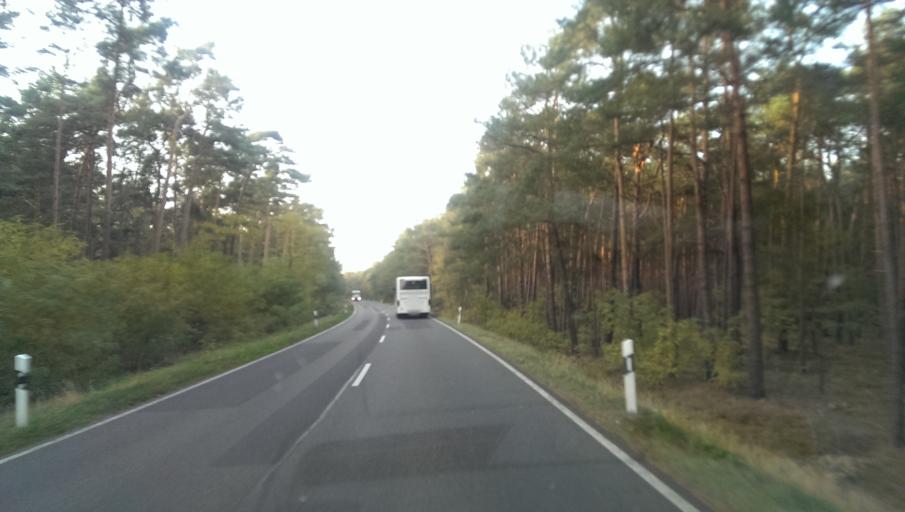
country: DE
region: Saxony-Anhalt
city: Holzdorf
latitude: 51.7803
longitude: 13.1950
